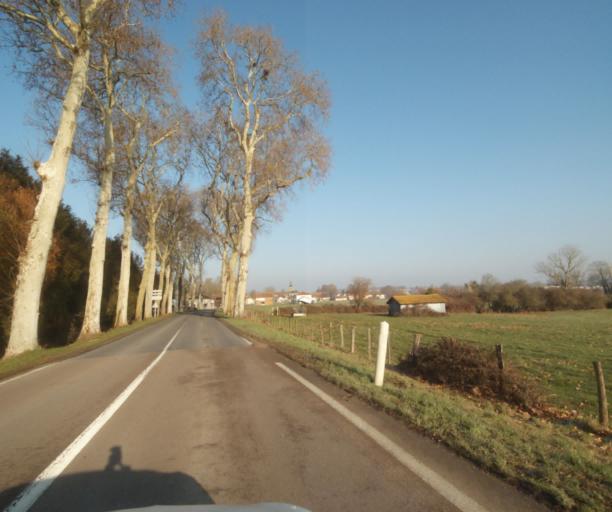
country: FR
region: Champagne-Ardenne
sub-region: Departement de la Haute-Marne
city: Montier-en-Der
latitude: 48.4659
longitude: 4.7638
